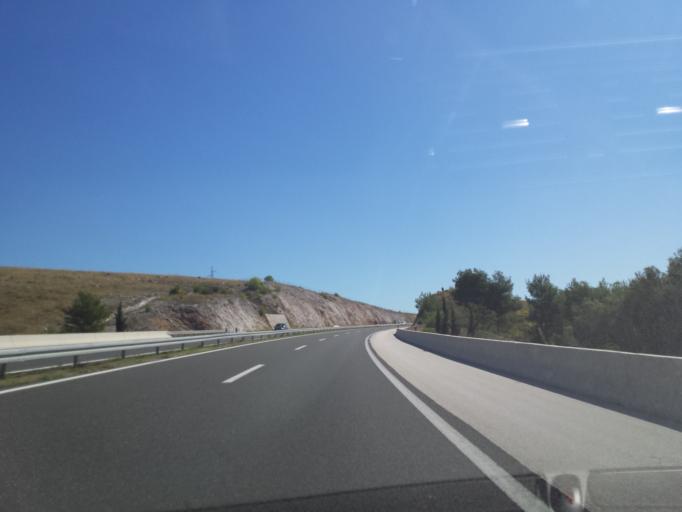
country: HR
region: Splitsko-Dalmatinska
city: Dugopolje
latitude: 43.6032
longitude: 16.6150
